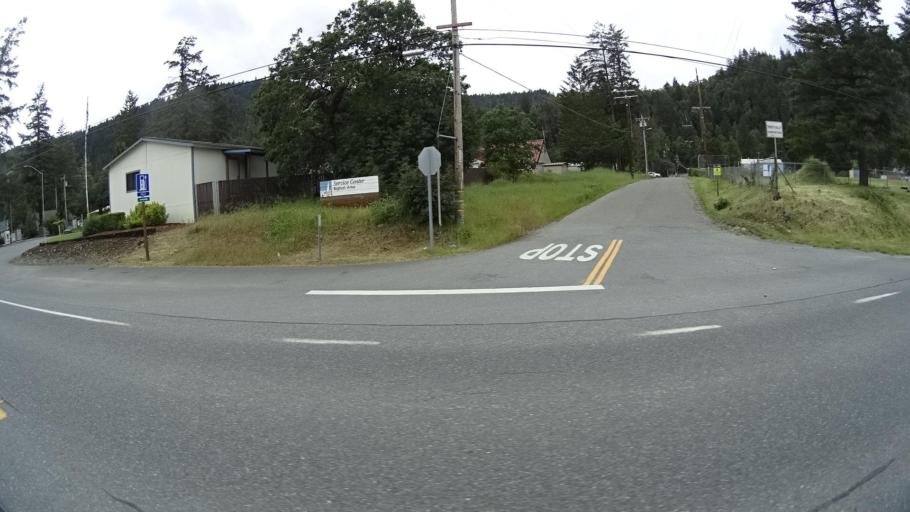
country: US
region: California
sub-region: Humboldt County
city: Willow Creek
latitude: 40.9479
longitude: -123.6367
